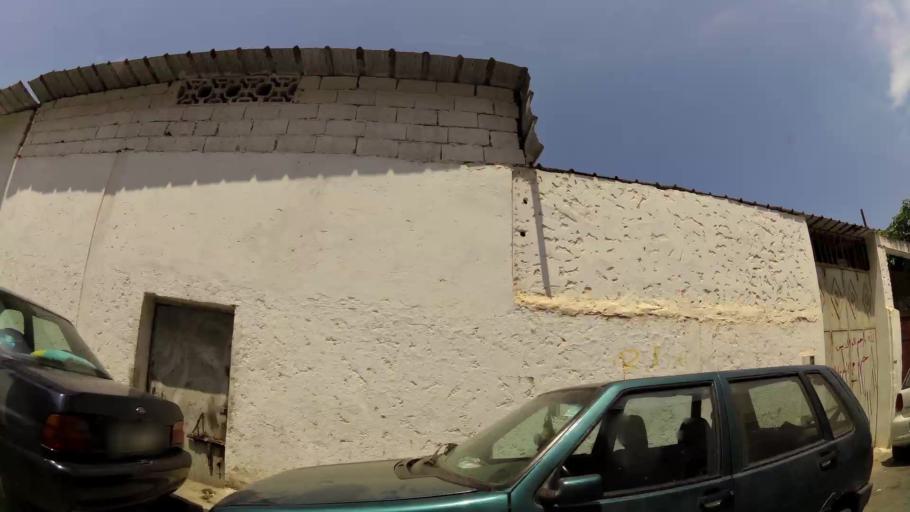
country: MA
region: Rabat-Sale-Zemmour-Zaer
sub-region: Skhirate-Temara
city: Temara
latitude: 33.9809
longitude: -6.8893
